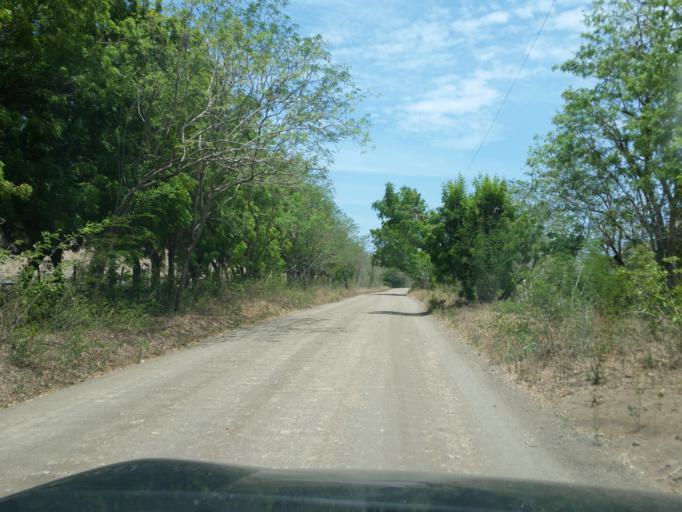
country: NI
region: Rivas
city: Tola
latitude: 11.5249
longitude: -86.0664
